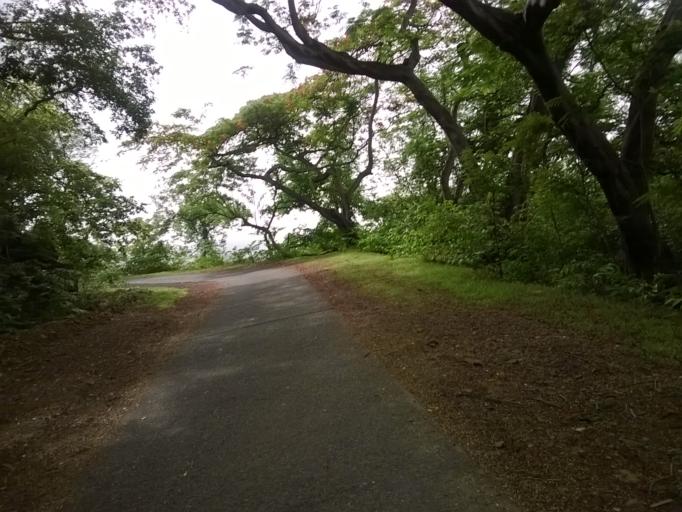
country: IN
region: Maharashtra
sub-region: Mumbai Suburban
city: Borivli
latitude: 19.2240
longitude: 72.8715
